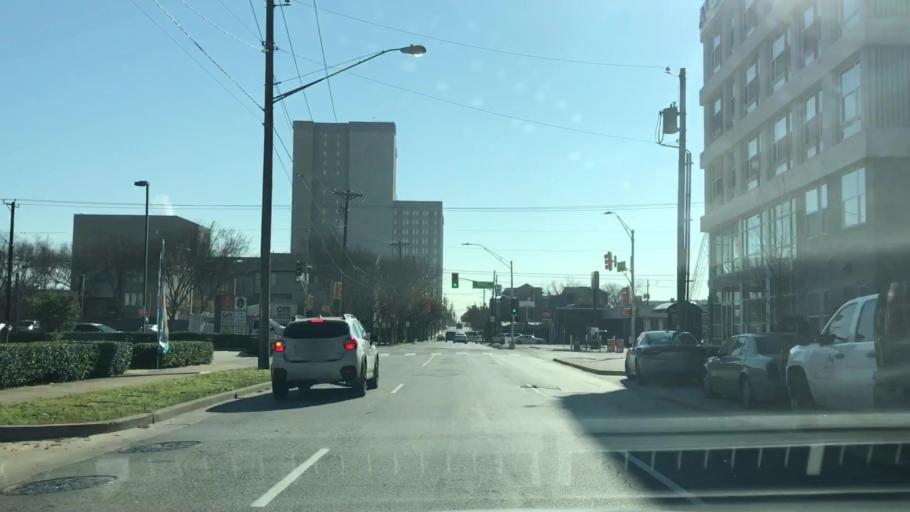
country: US
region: Texas
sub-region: Dallas County
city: Dallas
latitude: 32.8003
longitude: -96.7843
